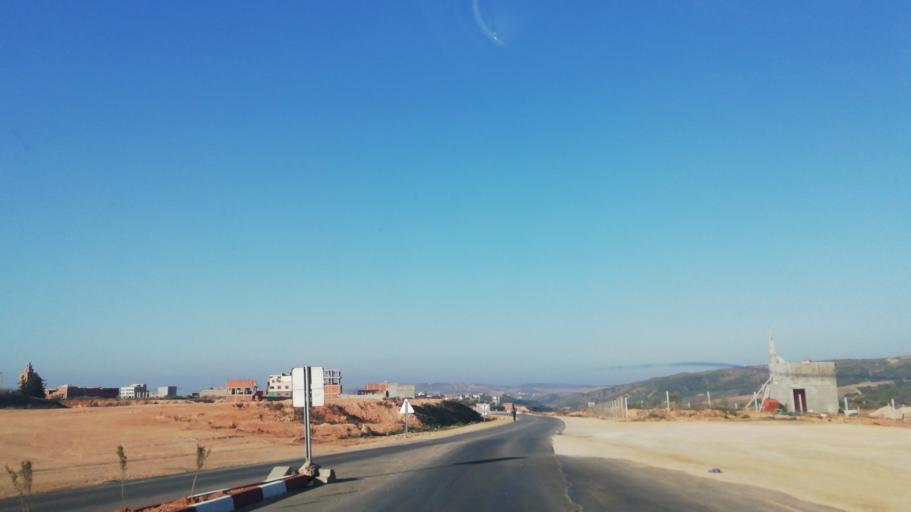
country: MA
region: Oriental
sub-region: Berkane-Taourirt
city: Ahfir
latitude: 35.0465
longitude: -2.1814
